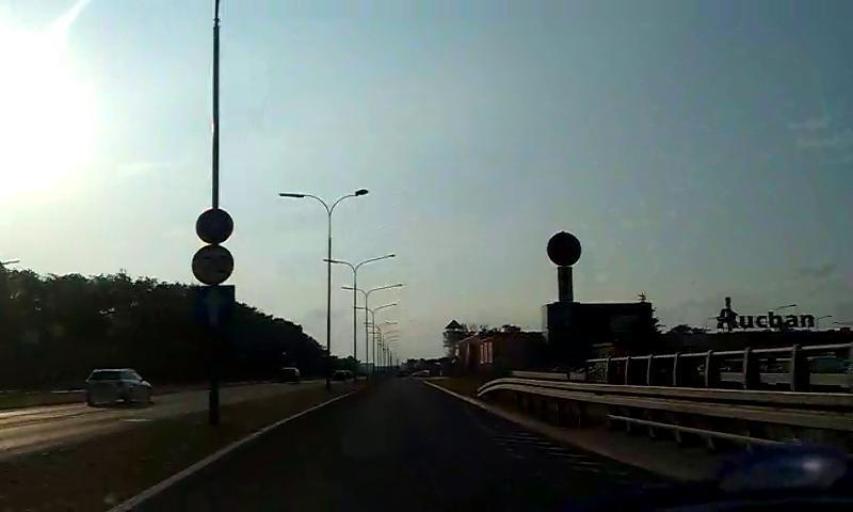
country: PL
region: Lublin Voivodeship
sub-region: Powiat lubelski
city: Jakubowice Murowane
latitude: 51.2301
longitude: 22.6143
